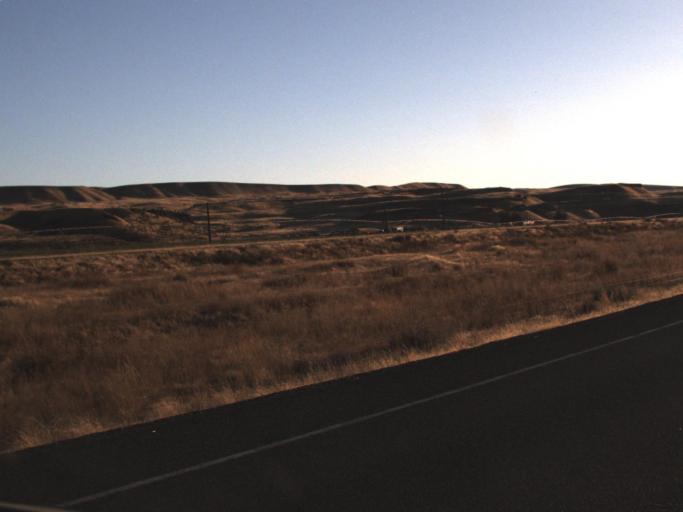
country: US
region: Washington
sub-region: Franklin County
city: Connell
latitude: 46.6677
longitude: -118.4765
